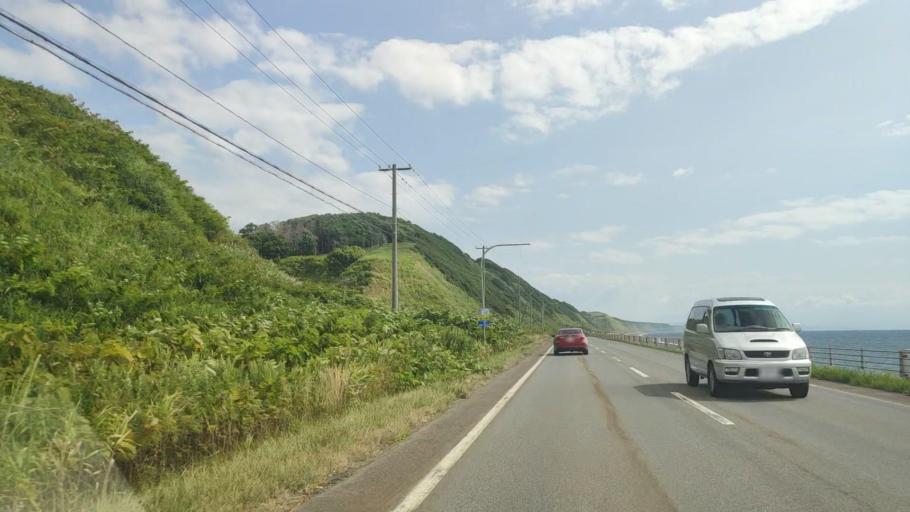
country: JP
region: Hokkaido
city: Rumoi
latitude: 44.0873
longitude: 141.6614
